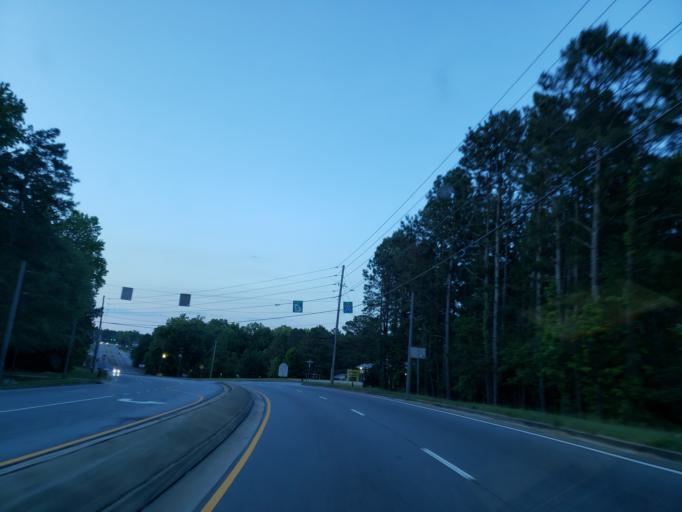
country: US
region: Georgia
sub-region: Douglas County
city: Douglasville
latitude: 33.7067
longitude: -84.7704
